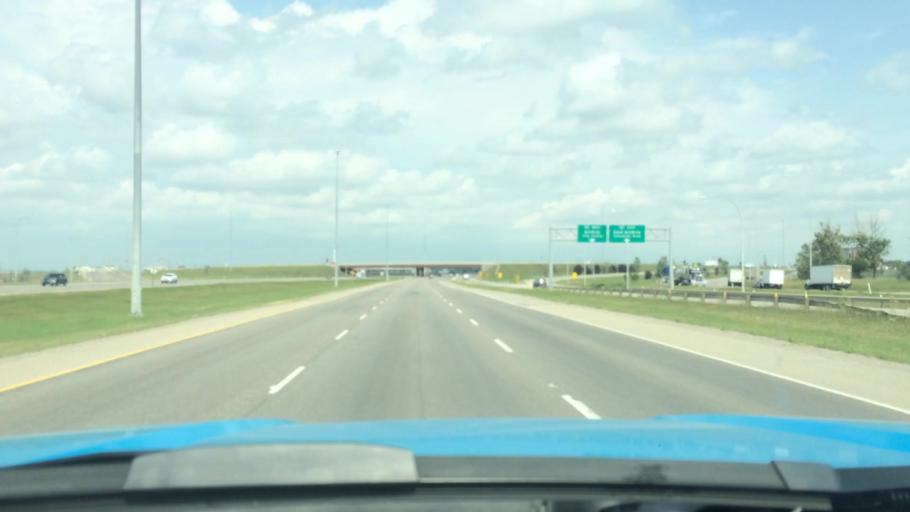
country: CA
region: Alberta
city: Airdrie
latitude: 51.2955
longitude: -114.0005
